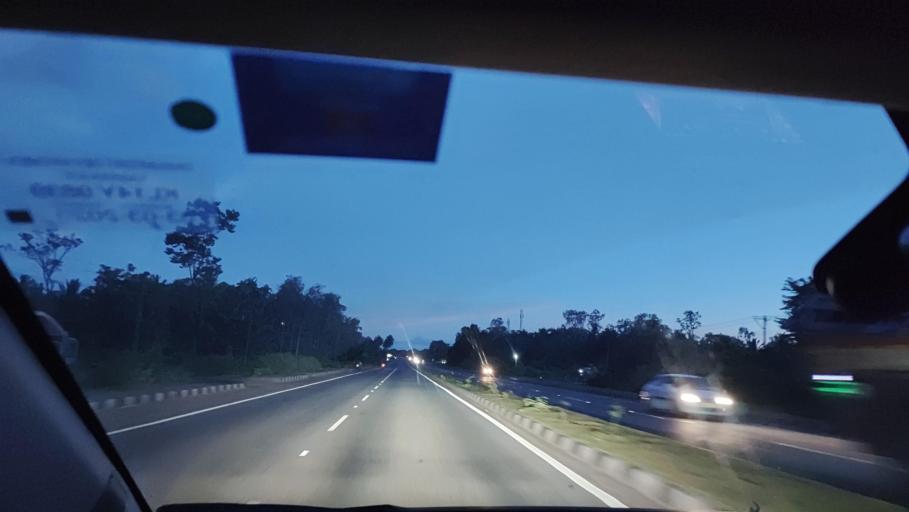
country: IN
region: Karnataka
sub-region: Uttar Kannada
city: Gokarna
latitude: 14.5526
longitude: 74.3924
